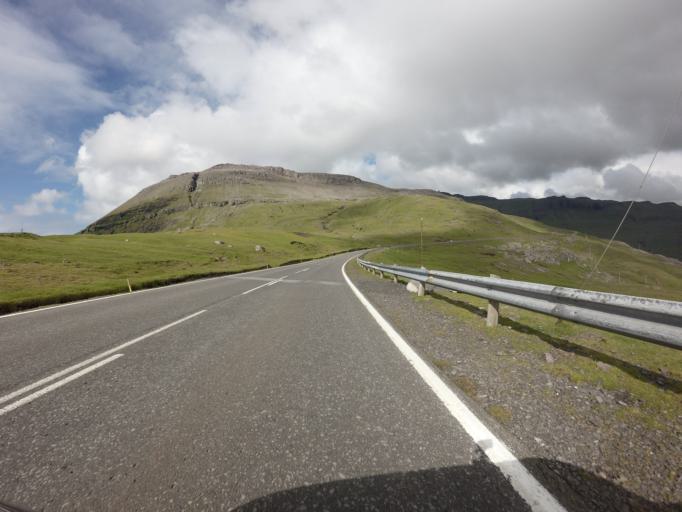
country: FO
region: Streymoy
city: Kollafjordhur
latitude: 62.0557
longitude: -6.9170
